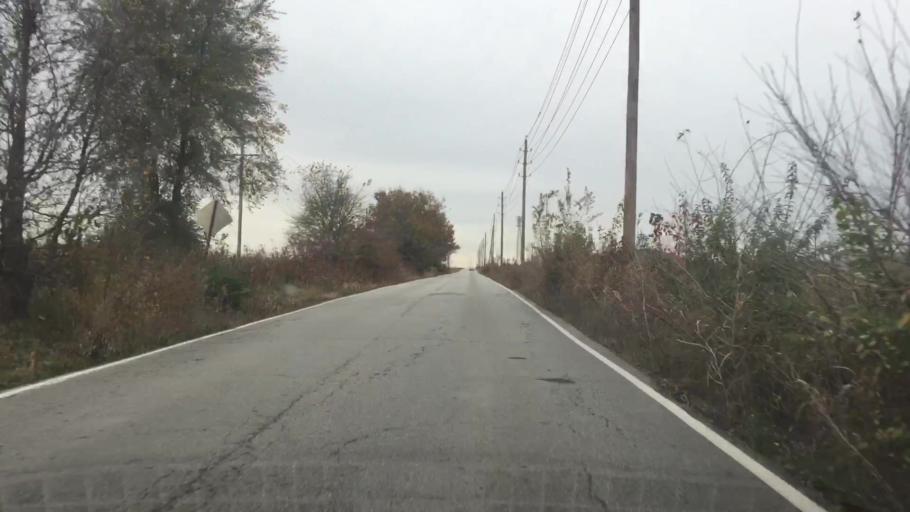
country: US
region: Missouri
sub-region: Cass County
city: Belton
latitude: 38.8007
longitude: -94.5130
